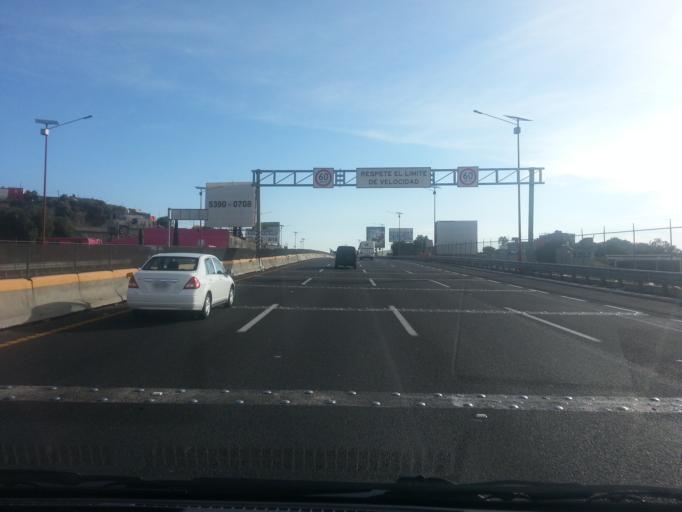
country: MX
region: Mexico
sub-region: Tlalnepantla de Baz
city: Puerto Escondido (Tepeolulco Puerto Escondido)
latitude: 19.5590
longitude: -99.0572
